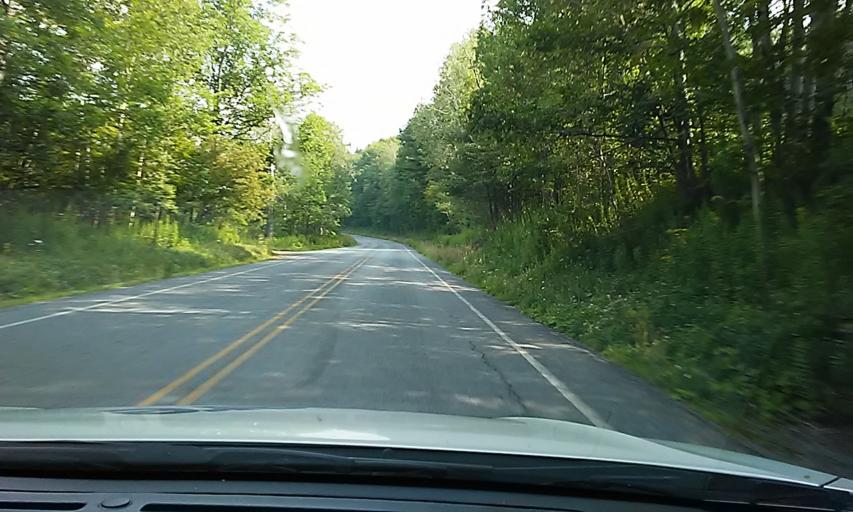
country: US
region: New York
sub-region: Allegany County
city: Wellsville
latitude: 41.9475
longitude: -77.8590
